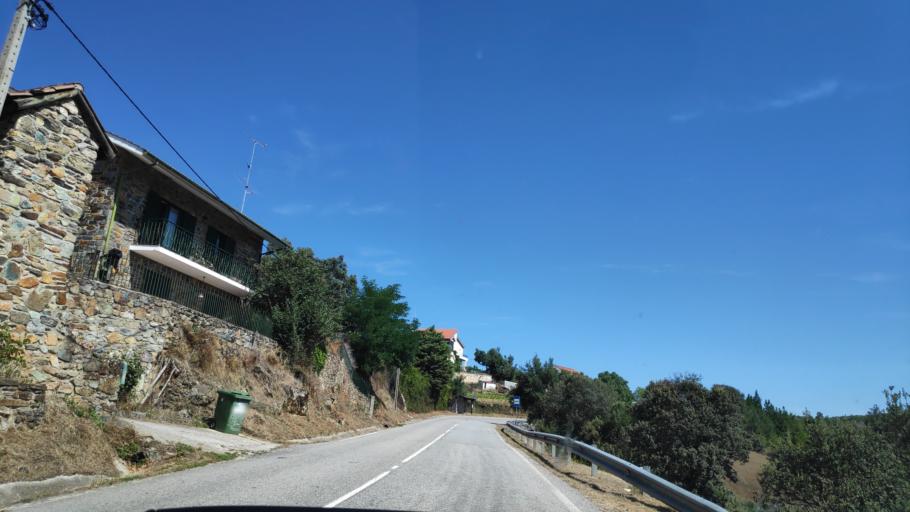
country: PT
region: Braganca
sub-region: Braganca Municipality
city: Braganca
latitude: 41.8371
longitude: -6.7468
